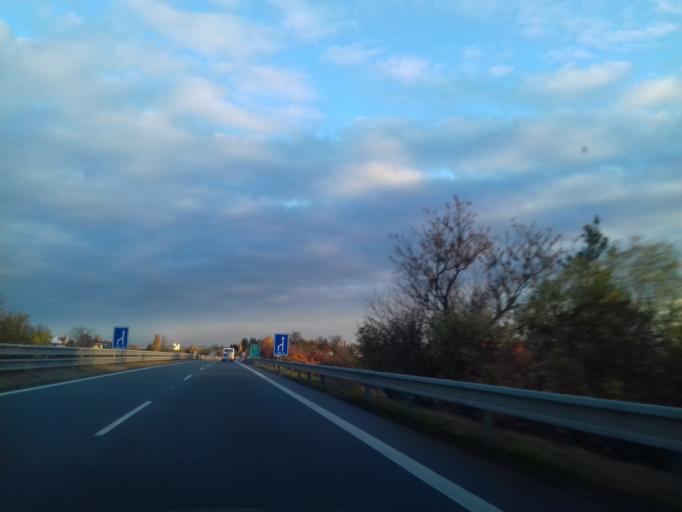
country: CZ
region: Olomoucky
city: Otaslavice
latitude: 49.3974
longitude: 17.1025
